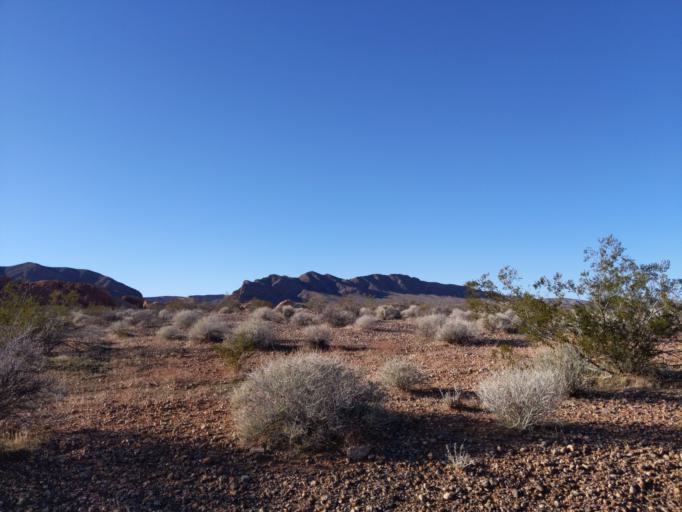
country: US
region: Nevada
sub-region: Clark County
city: Moapa Valley
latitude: 36.4237
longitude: -114.5532
